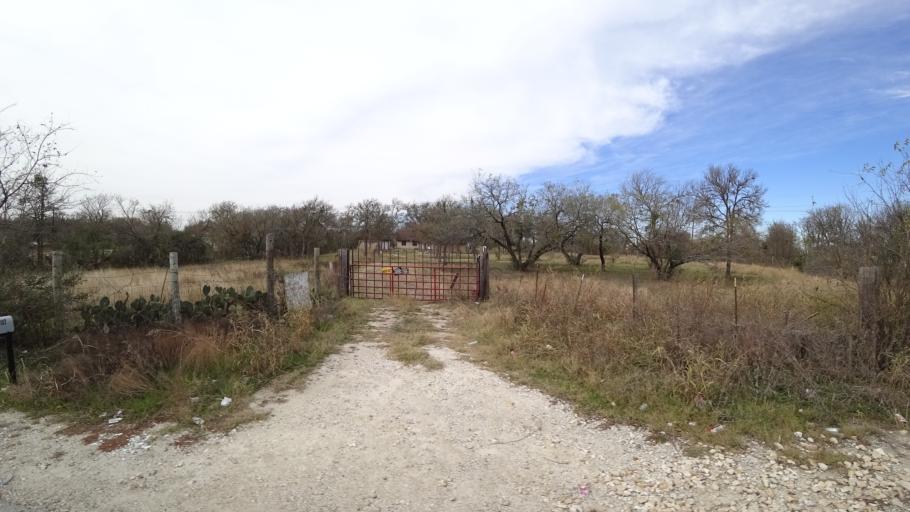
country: US
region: Texas
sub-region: Travis County
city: Garfield
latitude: 30.1397
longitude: -97.5682
